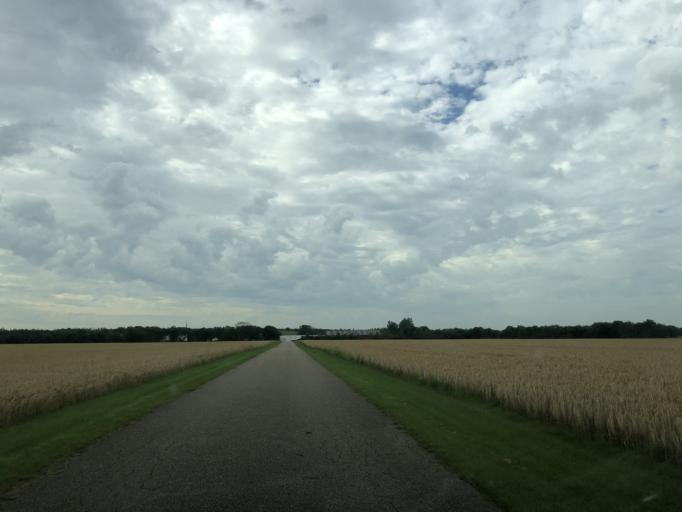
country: DK
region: Central Jutland
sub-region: Holstebro Kommune
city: Ulfborg
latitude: 56.3658
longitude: 8.4441
